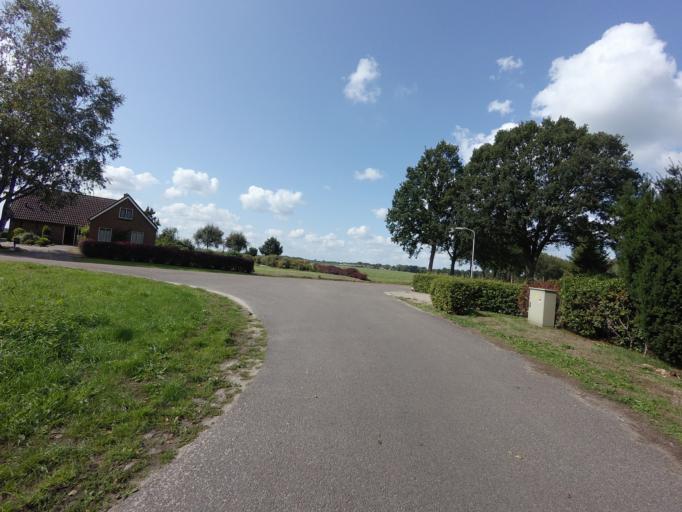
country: NL
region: Drenthe
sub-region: Gemeente Westerveld
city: Dwingeloo
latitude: 52.8490
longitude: 6.3955
